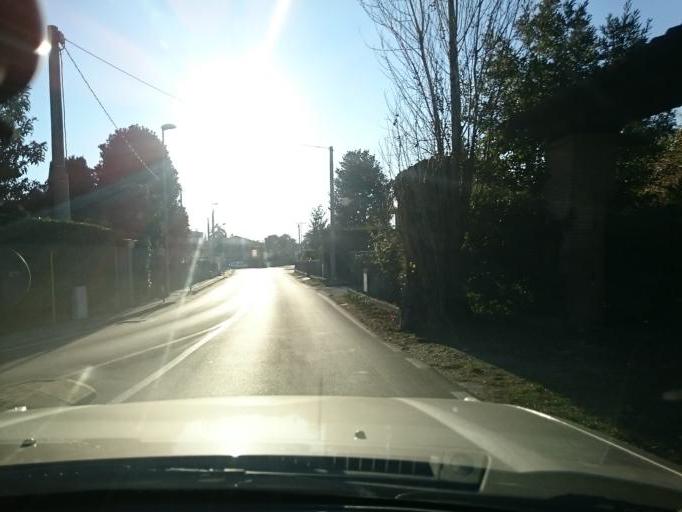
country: IT
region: Veneto
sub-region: Provincia di Padova
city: Noventa
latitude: 45.4127
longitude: 11.9450
